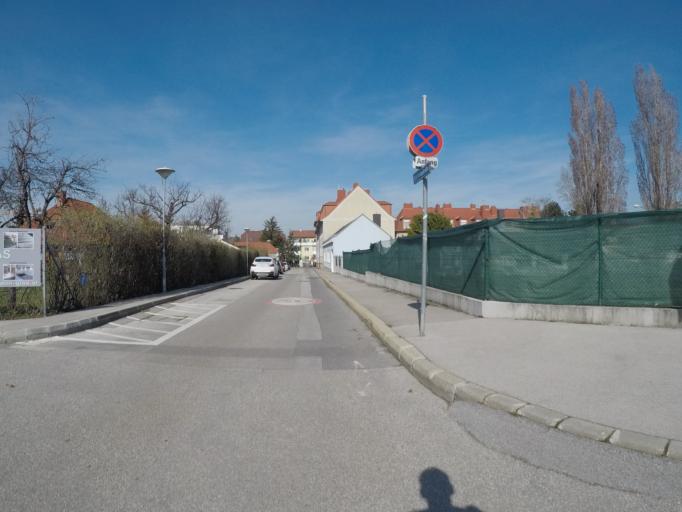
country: AT
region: Lower Austria
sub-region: Politischer Bezirk Modling
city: Vosendorf
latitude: 48.1195
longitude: 16.3390
